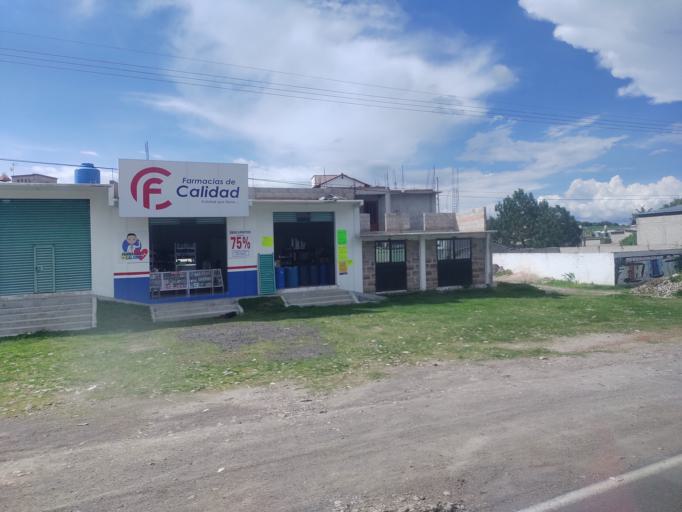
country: MX
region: Mexico
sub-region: Aculco
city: El Colorado
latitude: 20.0956
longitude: -99.7647
